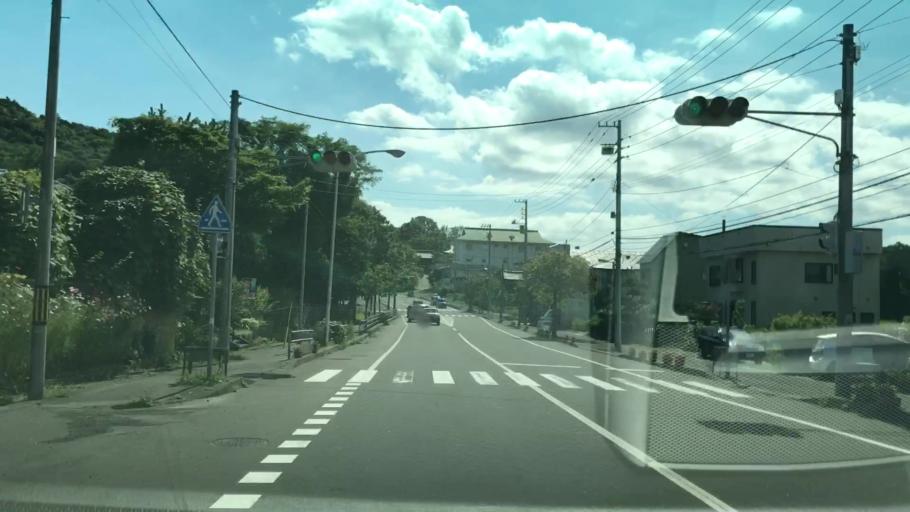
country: JP
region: Hokkaido
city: Muroran
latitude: 42.3203
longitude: 140.9966
